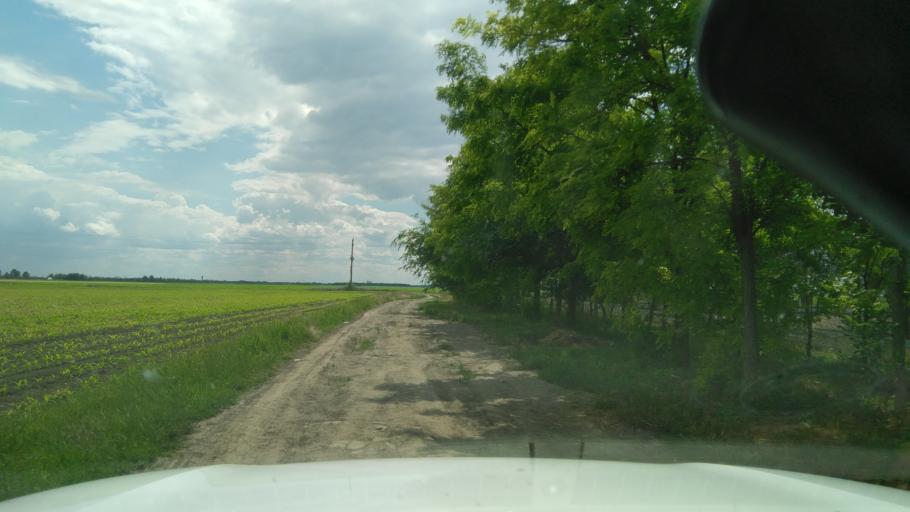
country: HU
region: Bekes
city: Magyarbanhegyes
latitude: 46.4561
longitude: 20.9521
